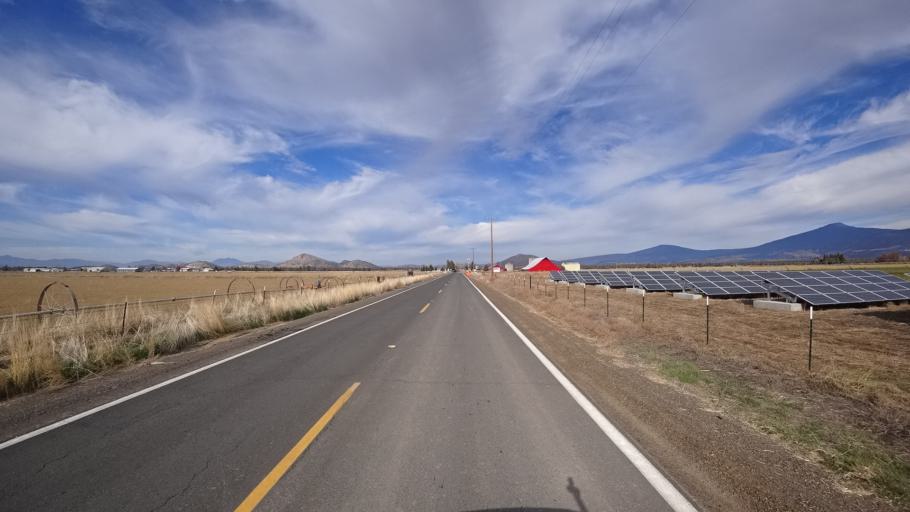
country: US
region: California
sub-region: Siskiyou County
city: Montague
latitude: 41.6194
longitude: -122.3997
